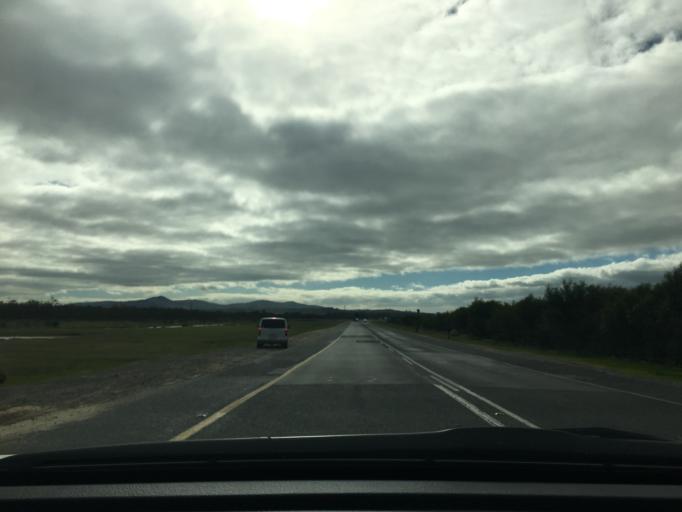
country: ZA
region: Western Cape
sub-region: Cape Winelands District Municipality
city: Stellenbosch
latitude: -34.0372
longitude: 18.7249
